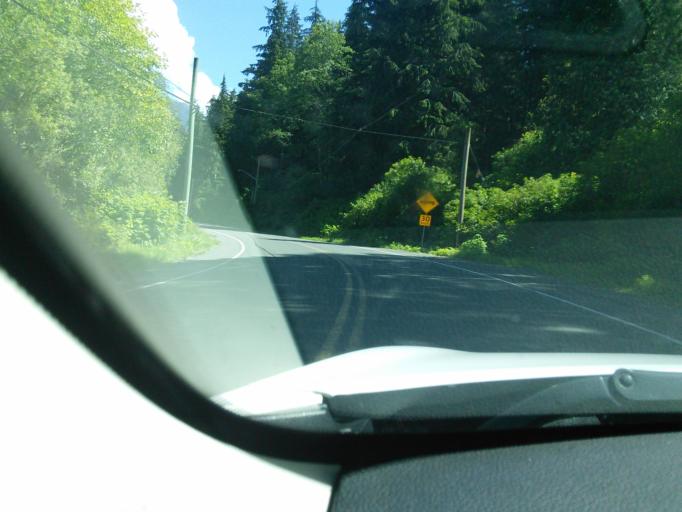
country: CA
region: British Columbia
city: Campbell River
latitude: 50.3640
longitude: -125.9357
